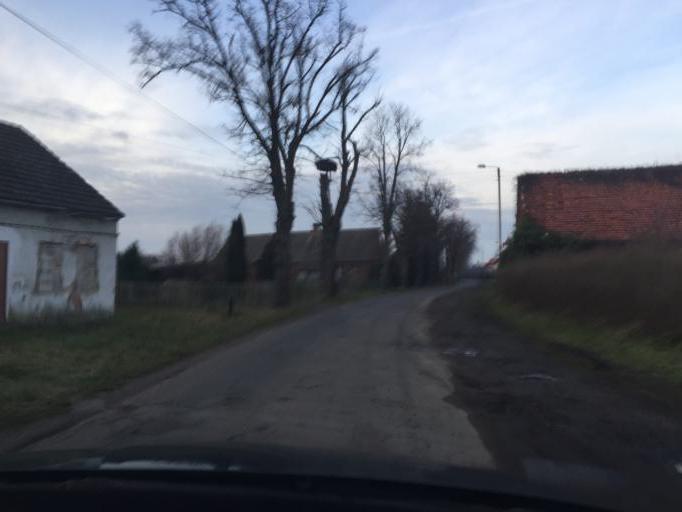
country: PL
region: Lubusz
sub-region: Powiat zielonogorski
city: Ochla
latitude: 51.8059
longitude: 15.4916
